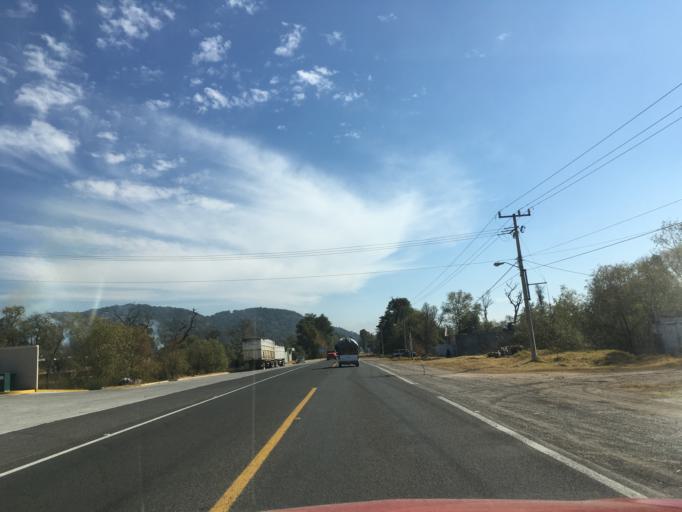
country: MX
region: Michoacan
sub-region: Hidalgo
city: Colonia Ecologica Asociacion de Lucha Social (Lucha Social)
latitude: 19.6978
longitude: -100.6073
